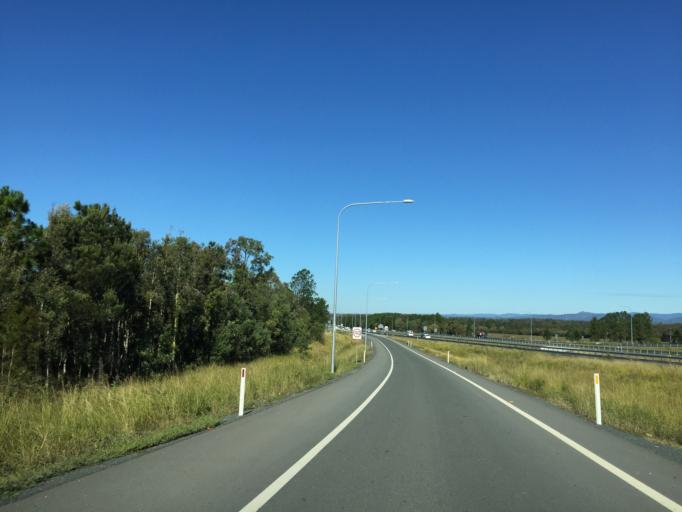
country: AU
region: Queensland
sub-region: Moreton Bay
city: Caboolture
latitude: -27.0417
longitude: 152.9785
